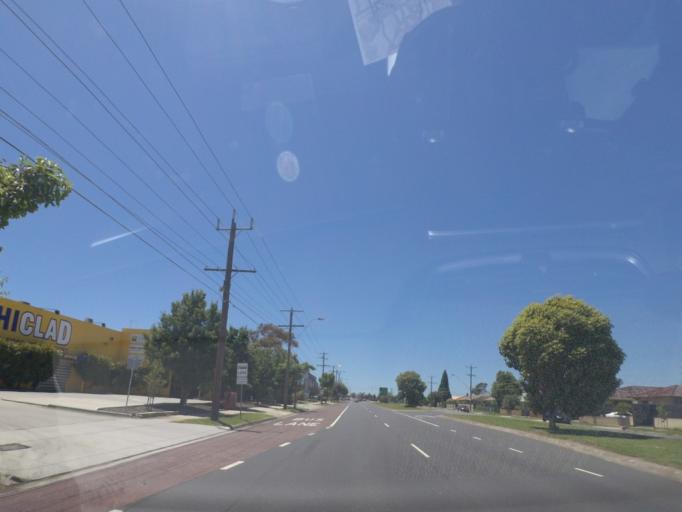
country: AU
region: Victoria
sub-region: Whittlesea
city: Thomastown
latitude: -37.6956
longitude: 145.0185
